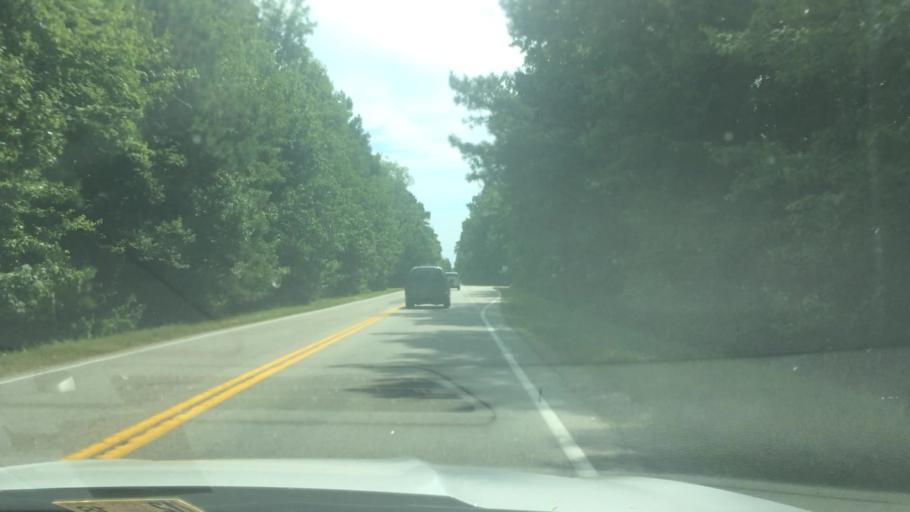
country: US
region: Virginia
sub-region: City of Poquoson
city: Poquoson
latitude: 37.1213
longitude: -76.4416
